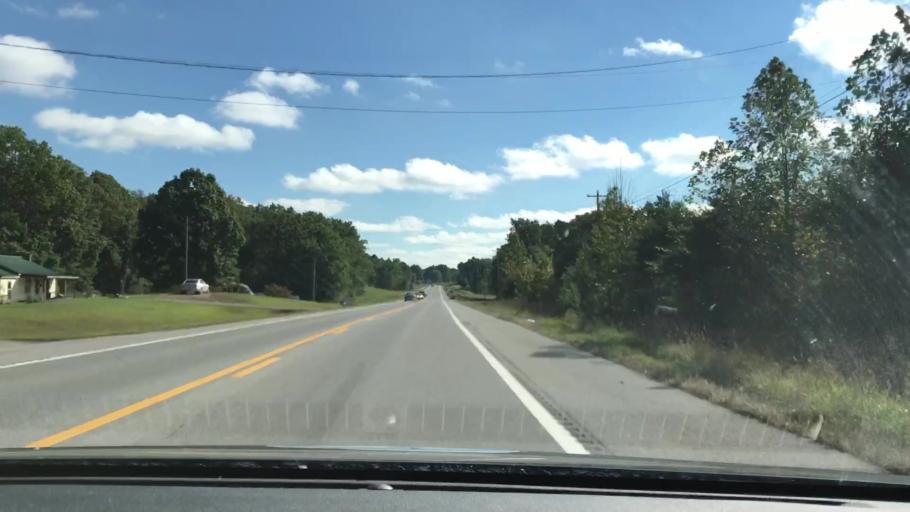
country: US
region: Tennessee
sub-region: Fentress County
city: Grimsley
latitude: 36.2995
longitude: -84.9746
